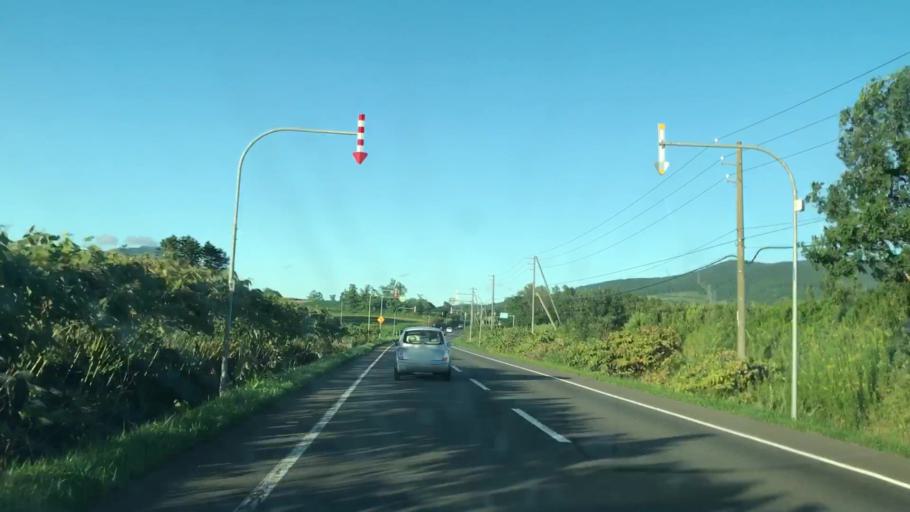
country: JP
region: Hokkaido
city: Niseko Town
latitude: 42.7013
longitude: 140.8480
